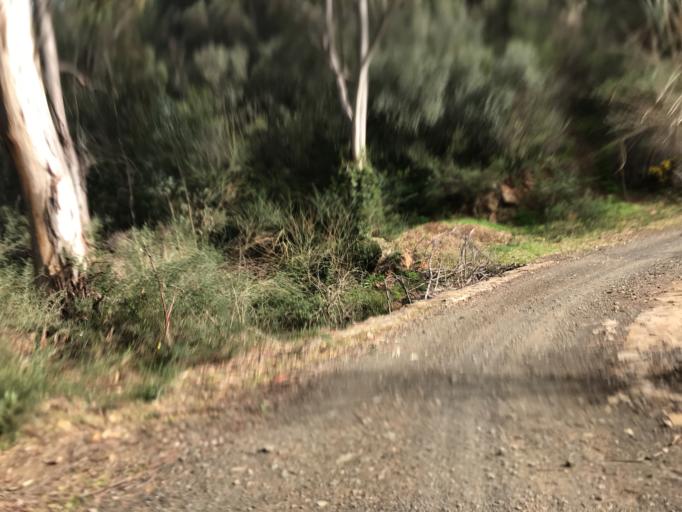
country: ES
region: Andalusia
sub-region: Provincia de Malaga
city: Malaga
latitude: 36.8064
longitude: -4.3983
